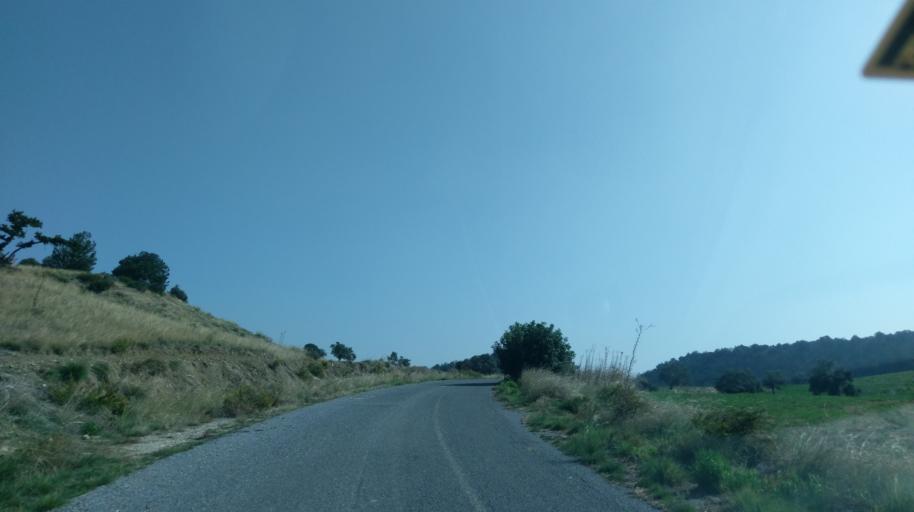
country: CY
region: Ammochostos
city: Lefkonoiko
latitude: 35.3212
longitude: 33.6720
